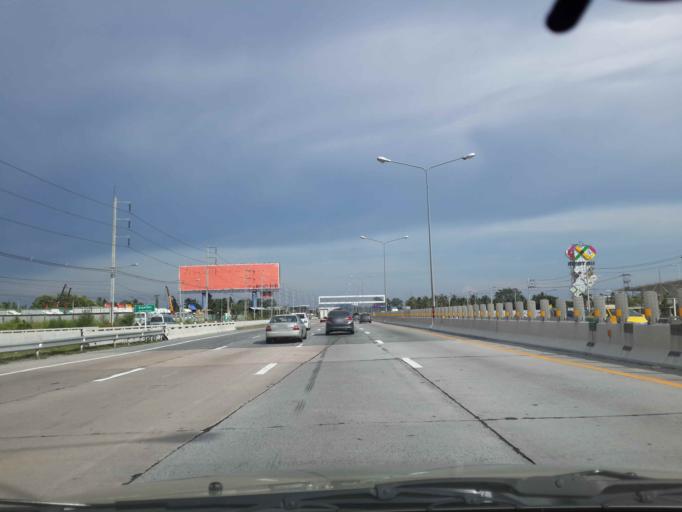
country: TH
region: Chon Buri
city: Si Racha
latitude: 13.2237
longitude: 101.0034
